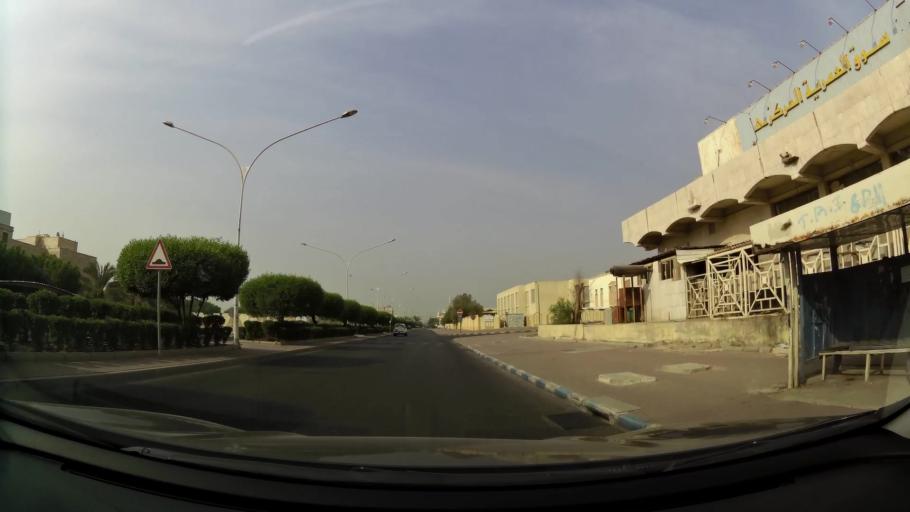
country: KW
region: Al Farwaniyah
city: Al Farwaniyah
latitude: 29.2950
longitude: 47.9539
